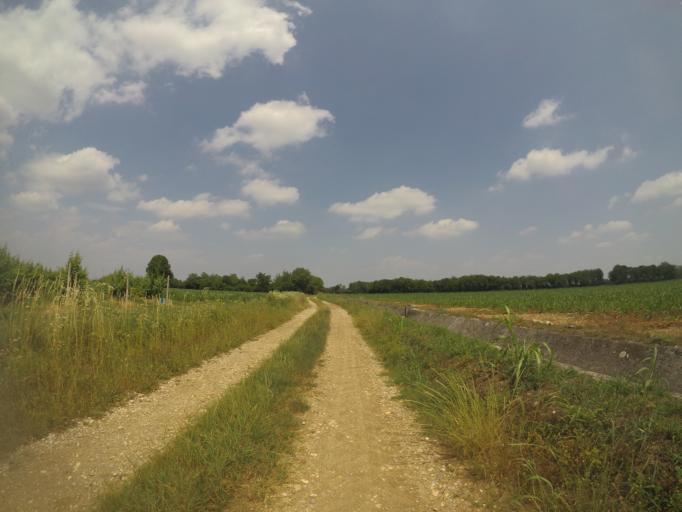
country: IT
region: Friuli Venezia Giulia
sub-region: Provincia di Udine
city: Bertiolo
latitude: 45.9572
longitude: 13.0611
